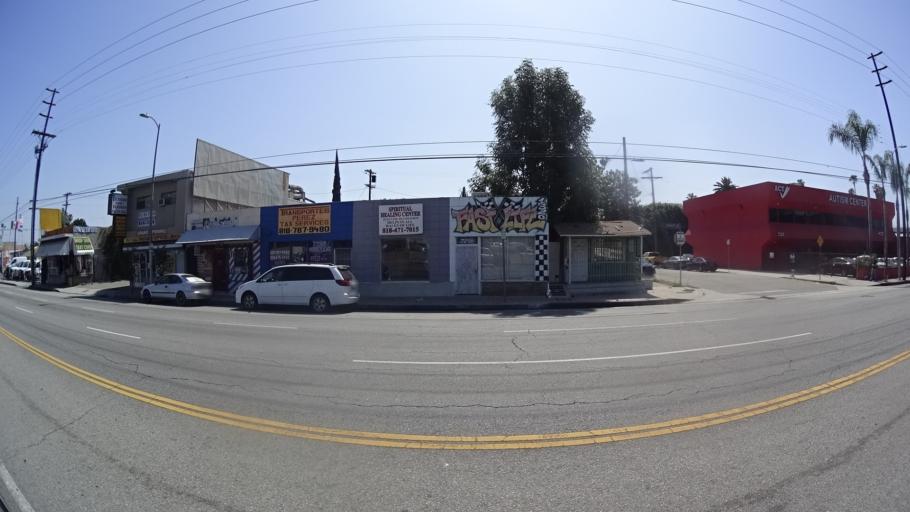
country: US
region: California
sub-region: Los Angeles County
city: Van Nuys
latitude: 34.2024
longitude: -118.4663
